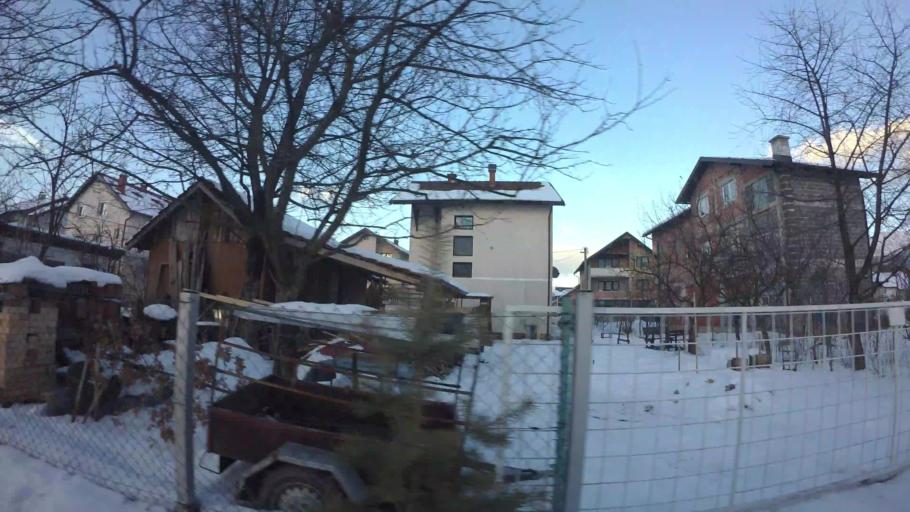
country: BA
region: Federation of Bosnia and Herzegovina
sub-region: Kanton Sarajevo
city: Sarajevo
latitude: 43.8085
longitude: 18.3684
